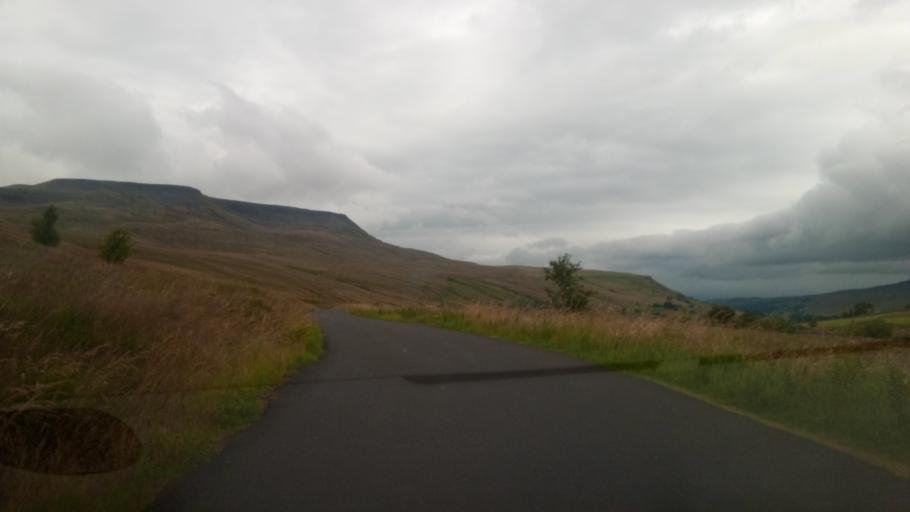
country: GB
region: England
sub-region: Cumbria
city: Kirkby Stephen
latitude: 54.3641
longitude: -2.3470
